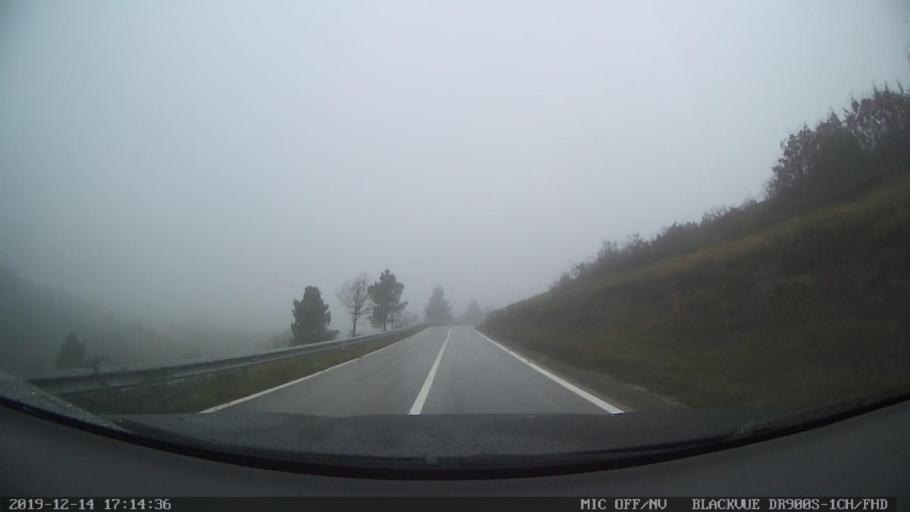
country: PT
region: Vila Real
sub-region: Vila Pouca de Aguiar
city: Vila Pouca de Aguiar
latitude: 41.5012
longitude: -7.6270
